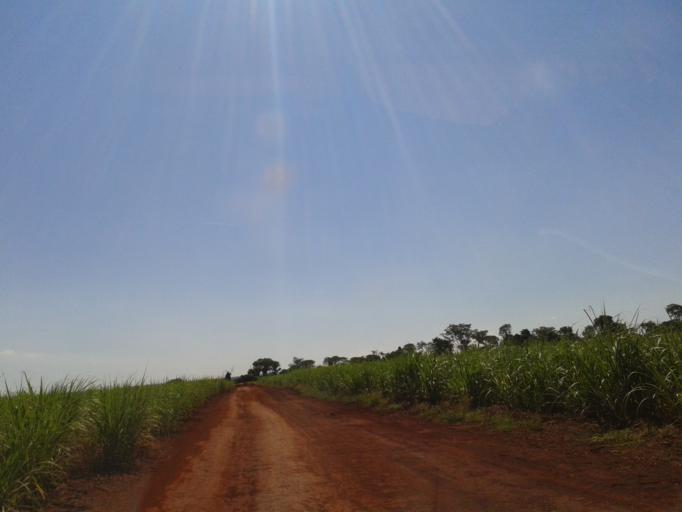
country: BR
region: Minas Gerais
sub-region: Centralina
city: Centralina
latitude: -18.6213
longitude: -49.2700
